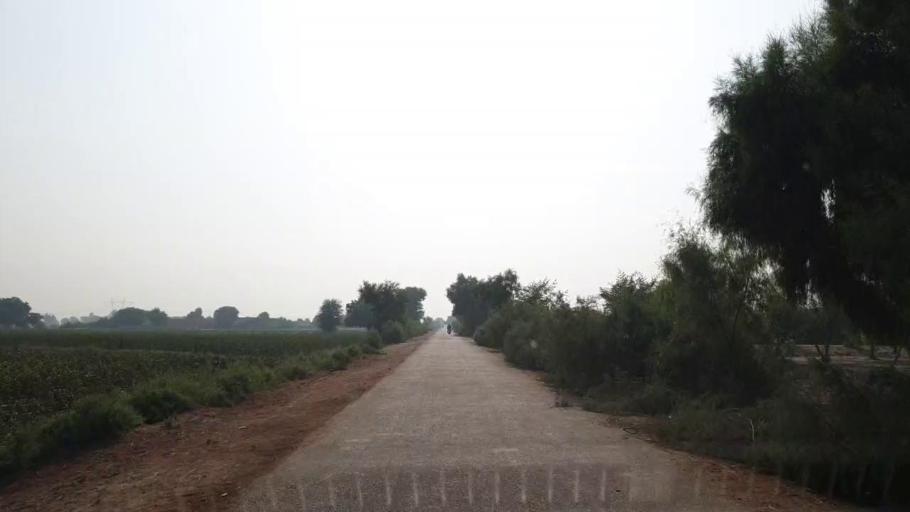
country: PK
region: Sindh
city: Bhan
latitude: 26.4815
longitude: 67.7698
